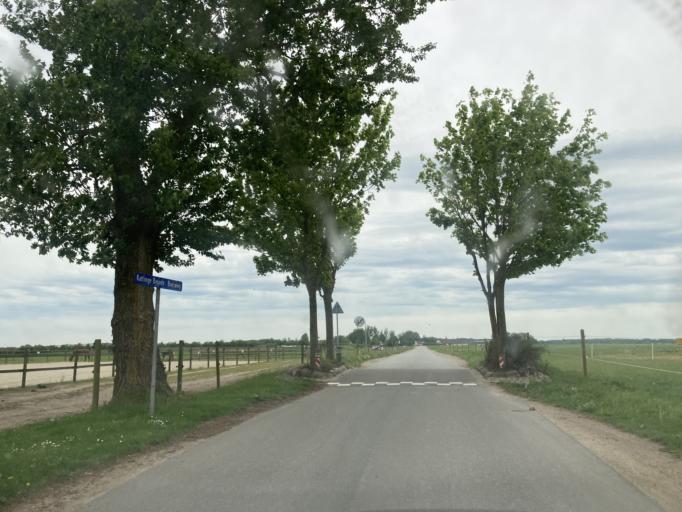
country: DK
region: Zealand
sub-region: Roskilde Kommune
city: Svogerslev
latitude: 55.6574
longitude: 11.9982
